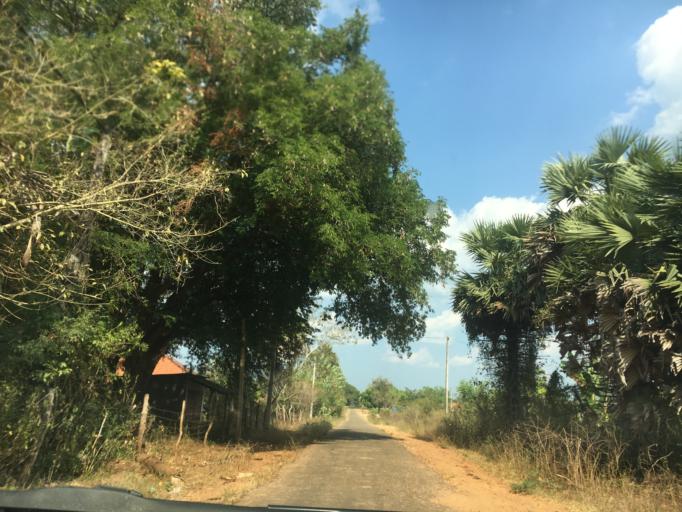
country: LK
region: Northern Province
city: Kilinochchi
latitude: 9.1403
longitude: 80.4450
